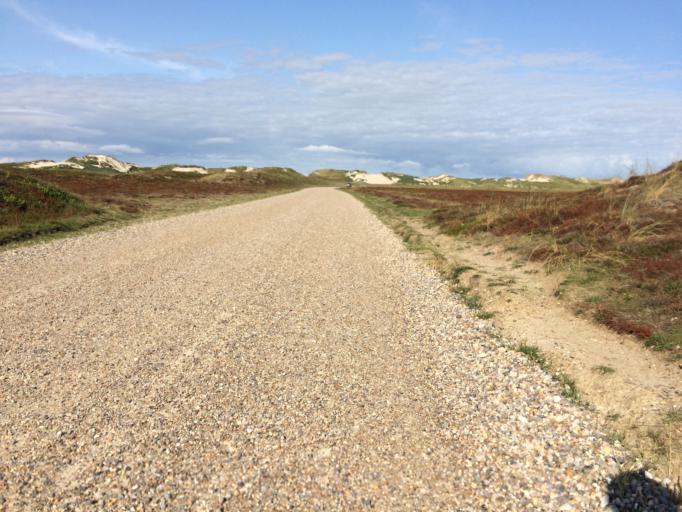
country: DK
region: Central Jutland
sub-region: Ringkobing-Skjern Kommune
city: Hvide Sande
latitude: 55.8964
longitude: 8.1624
